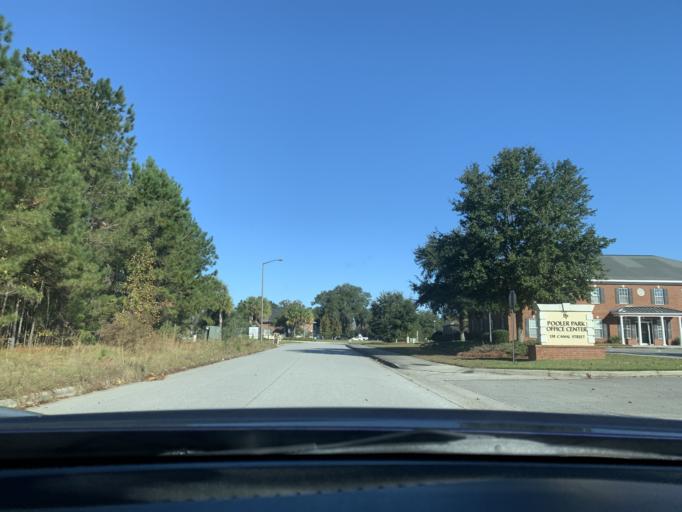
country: US
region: Georgia
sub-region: Chatham County
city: Pooler
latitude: 32.1301
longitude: -81.2553
